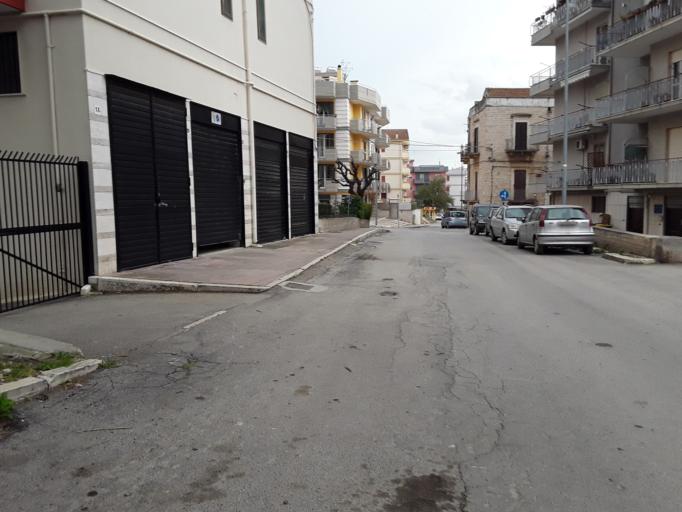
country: IT
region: Apulia
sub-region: Provincia di Bari
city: Ruvo di Puglia
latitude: 41.1193
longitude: 16.4787
